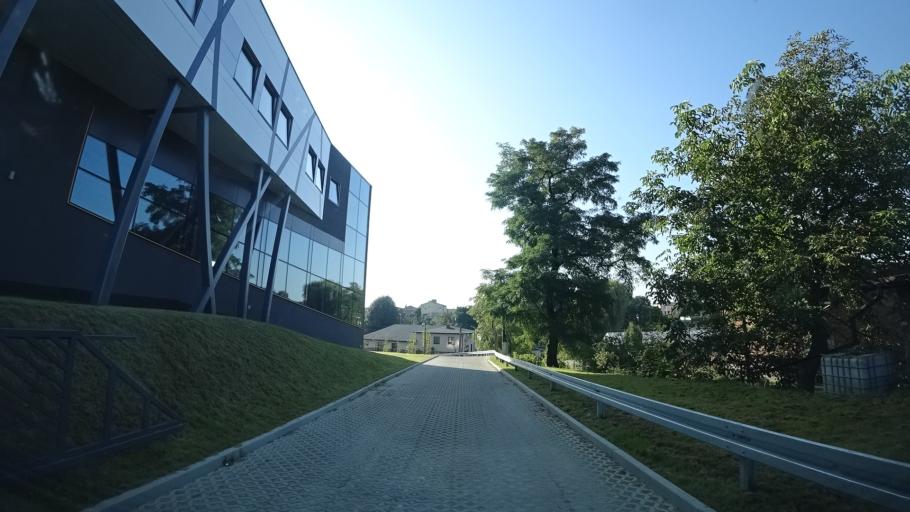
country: PL
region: Silesian Voivodeship
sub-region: Zory
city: Zory
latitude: 50.0359
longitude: 18.6534
